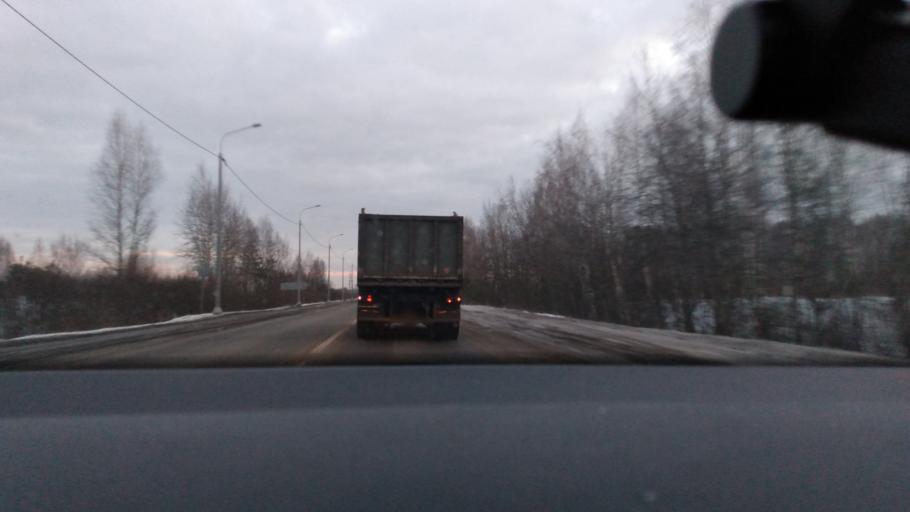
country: RU
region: Moskovskaya
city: Yegor'yevsk
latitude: 55.4127
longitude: 39.0483
